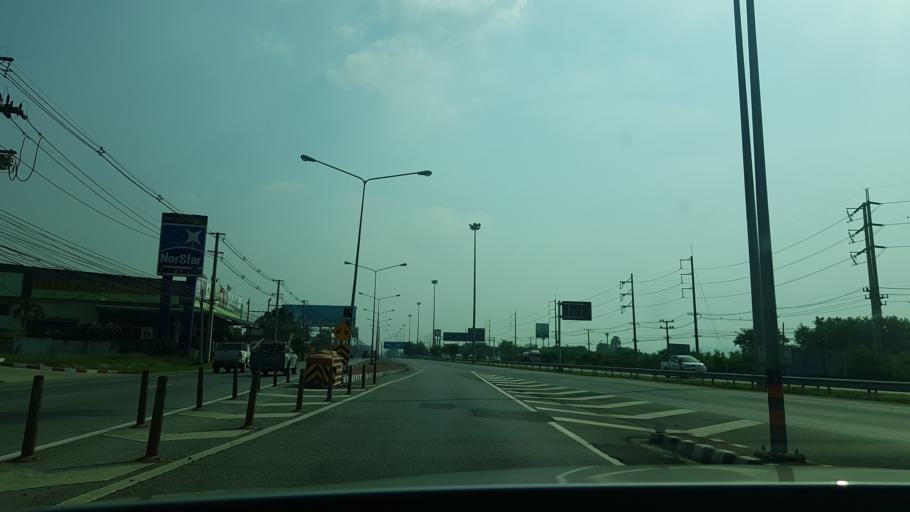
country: TH
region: Ratchaburi
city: Pak Tho
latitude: 13.3328
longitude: 99.8301
